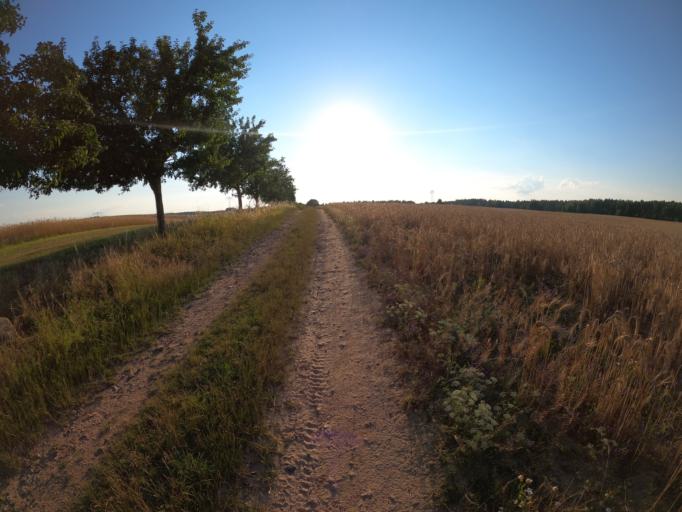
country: DE
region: Brandenburg
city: Althuttendorf
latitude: 53.0345
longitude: 13.8736
